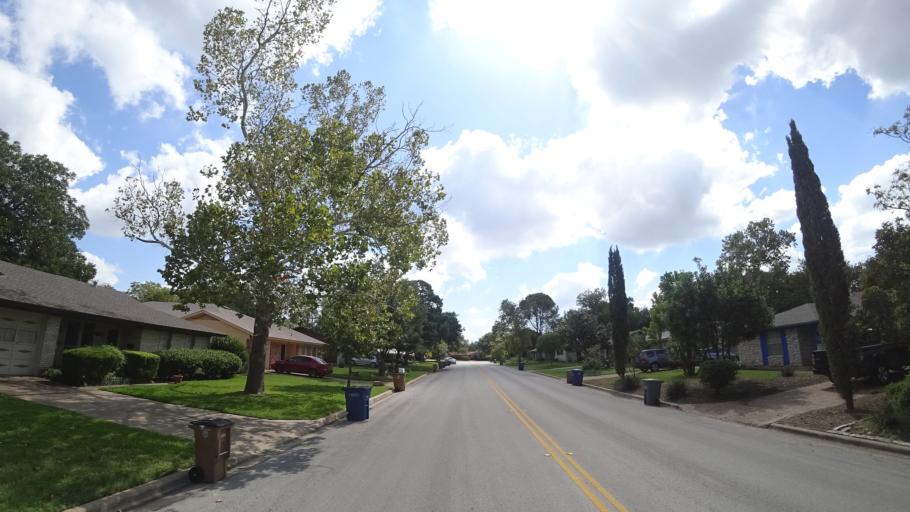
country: US
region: Texas
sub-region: Travis County
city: Wells Branch
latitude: 30.3631
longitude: -97.7219
